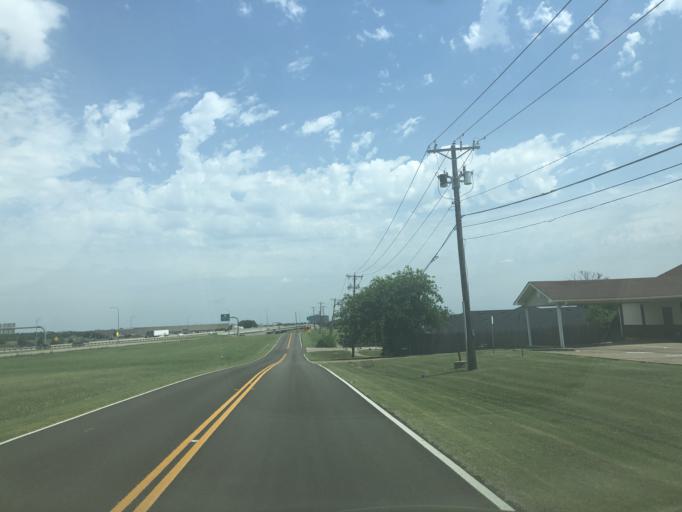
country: US
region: Texas
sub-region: Dallas County
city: Grand Prairie
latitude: 32.7239
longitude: -97.0196
